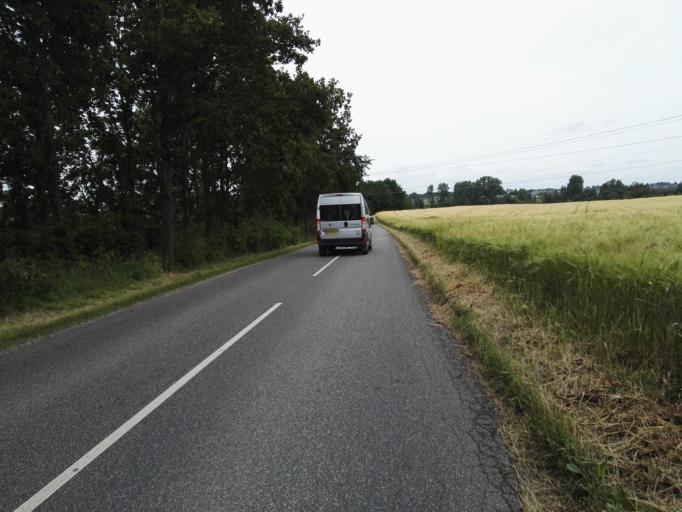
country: DK
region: Capital Region
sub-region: Egedal Kommune
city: Vekso
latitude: 55.7316
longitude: 12.2360
